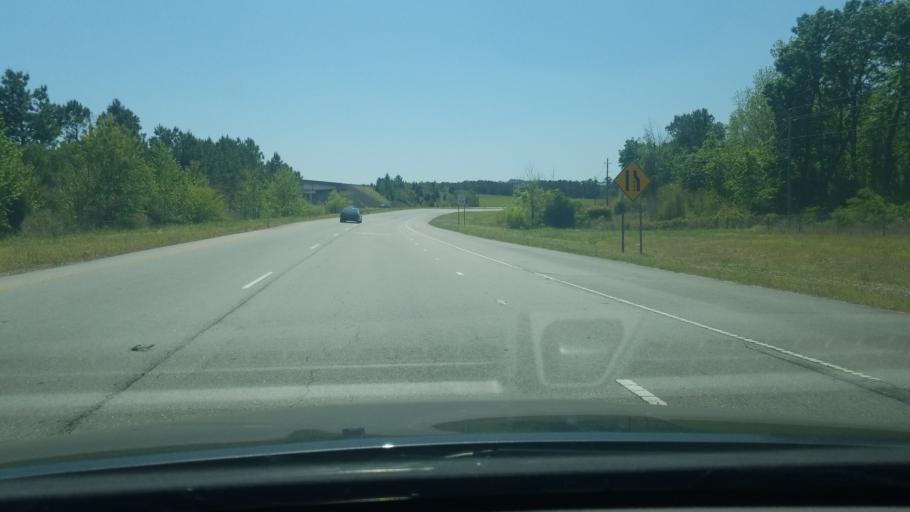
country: US
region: North Carolina
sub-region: Onslow County
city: Jacksonville
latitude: 34.7426
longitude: -77.4586
